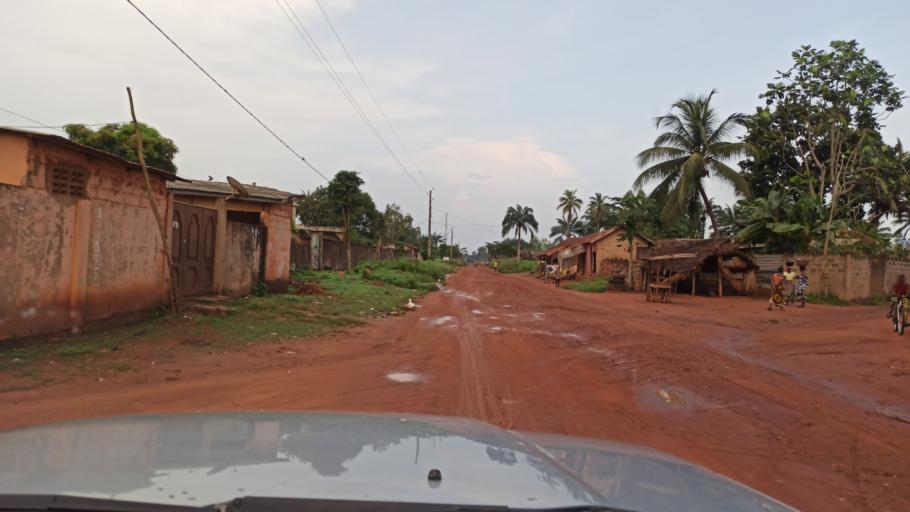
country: BJ
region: Queme
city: Porto-Novo
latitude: 6.4943
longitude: 2.6907
